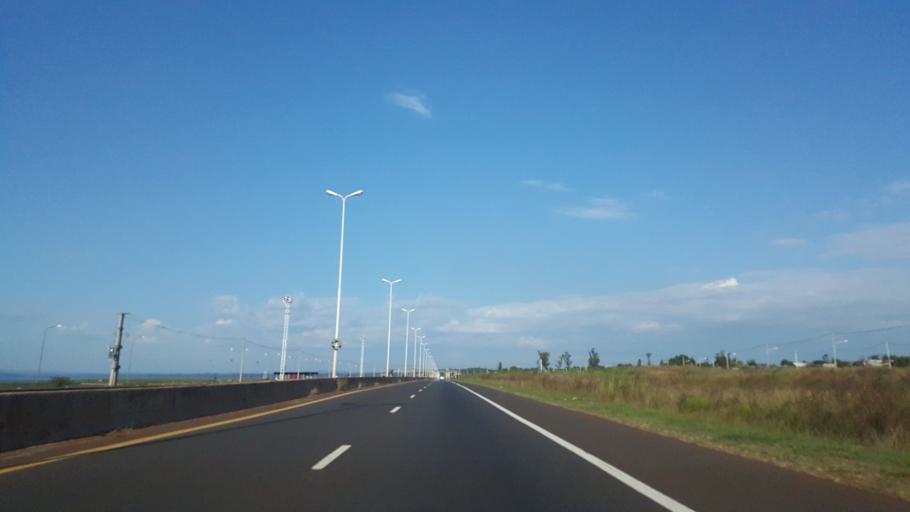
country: AR
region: Misiones
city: Garupa
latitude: -27.4295
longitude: -55.8688
